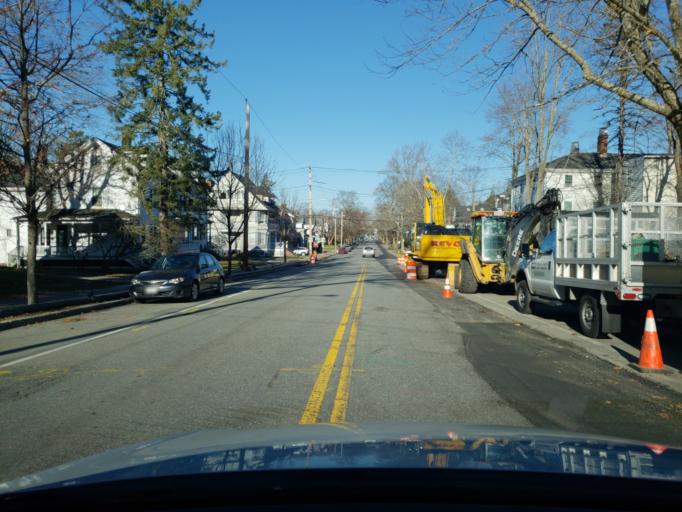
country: US
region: Massachusetts
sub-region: Essex County
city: Andover
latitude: 42.6508
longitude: -71.1367
